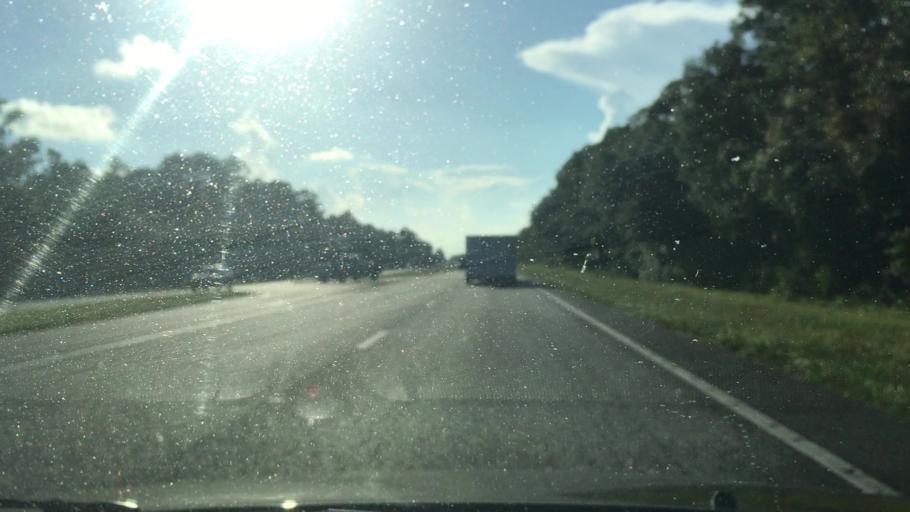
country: US
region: Florida
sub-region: Orange County
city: Christmas
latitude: 28.5368
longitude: -81.0119
